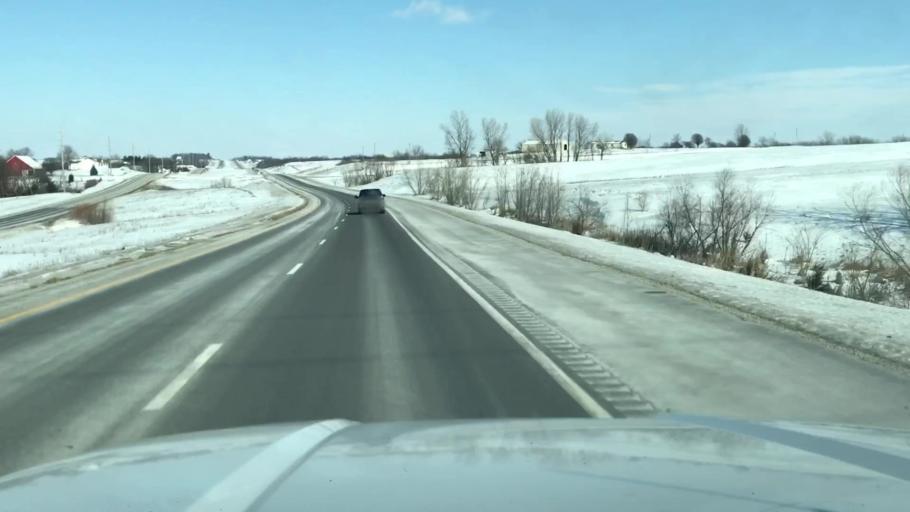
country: US
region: Missouri
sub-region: Nodaway County
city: Maryville
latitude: 40.1825
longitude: -94.8681
